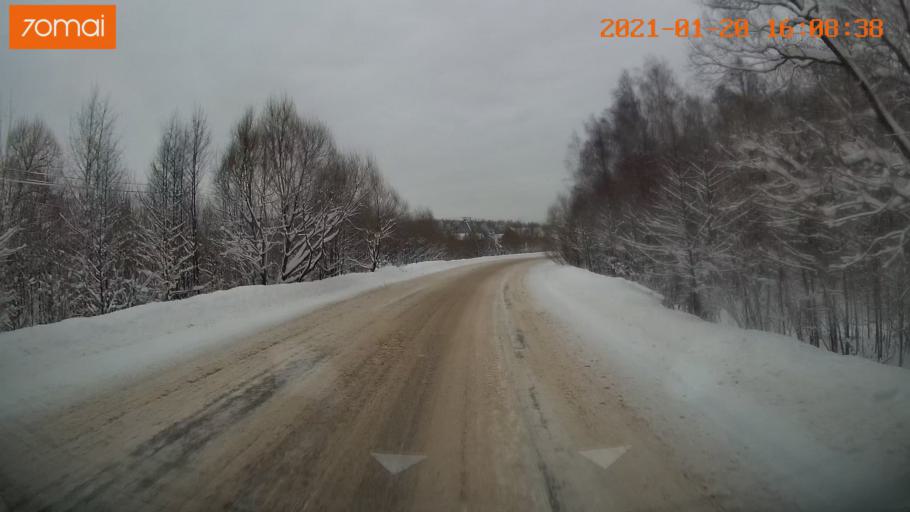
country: RU
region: Vladimir
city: Sudogda
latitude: 56.0774
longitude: 40.7675
